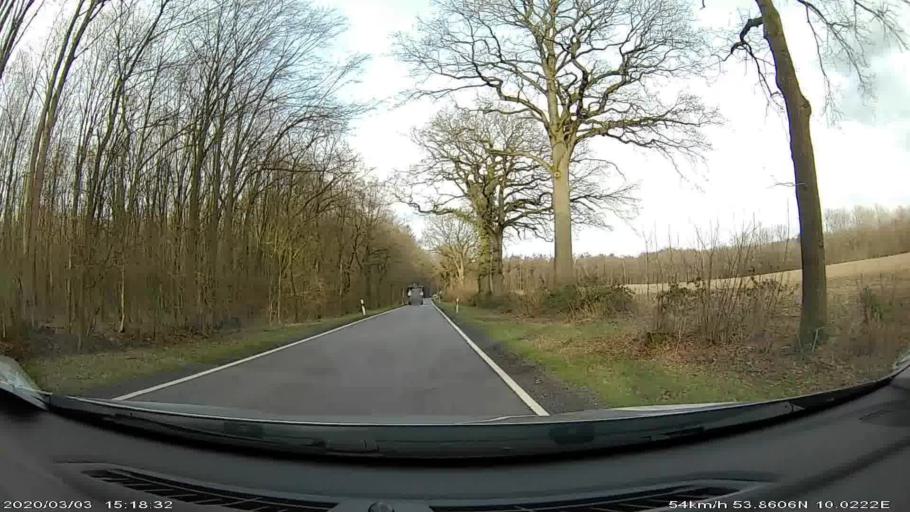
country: DE
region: Schleswig-Holstein
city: Kattendorf
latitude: 53.8601
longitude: 10.0220
